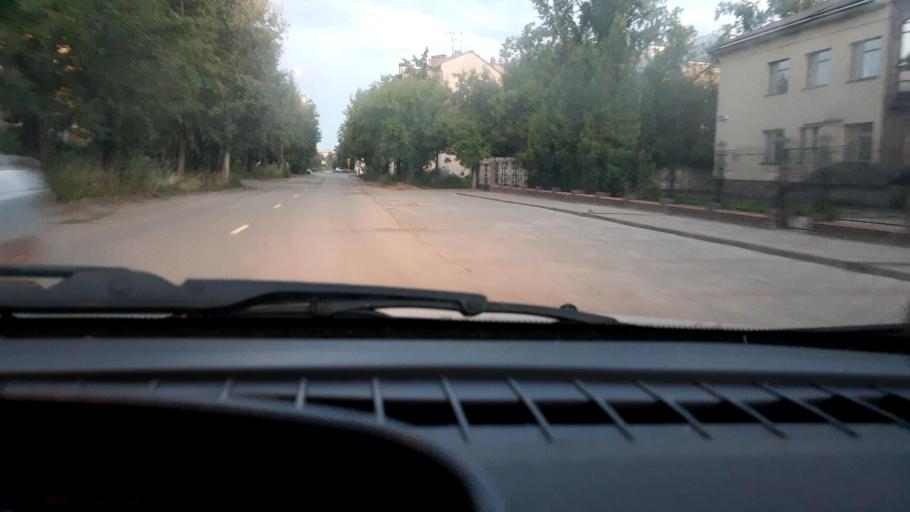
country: RU
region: Nizjnij Novgorod
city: Dzerzhinsk
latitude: 56.2407
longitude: 43.4791
